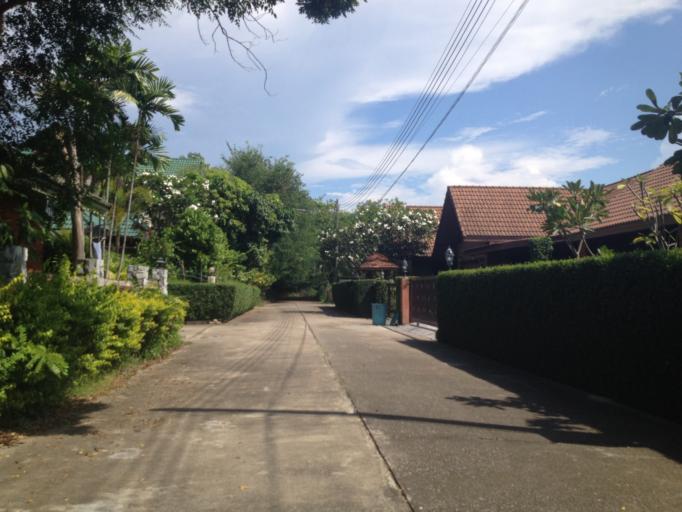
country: TH
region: Chiang Mai
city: Hang Dong
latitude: 18.7370
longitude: 98.9374
